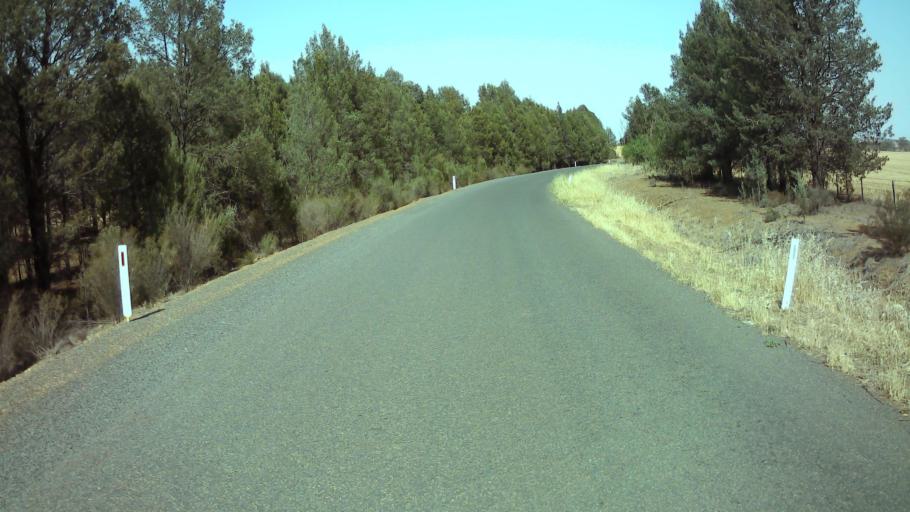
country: AU
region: New South Wales
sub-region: Weddin
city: Grenfell
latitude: -33.8712
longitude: 148.1028
